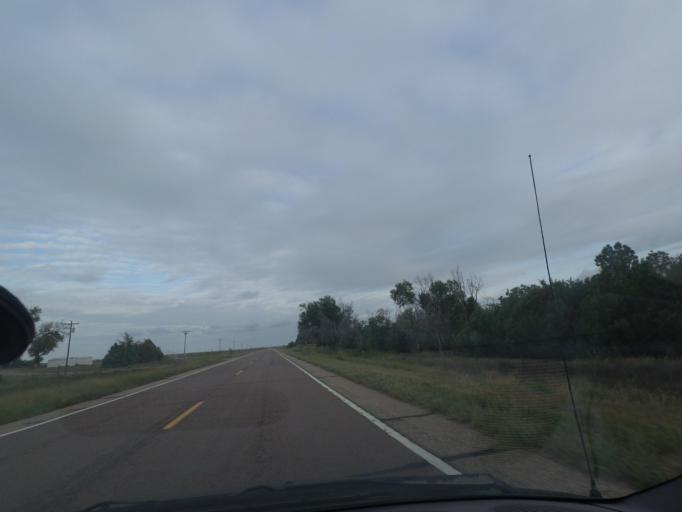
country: US
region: Colorado
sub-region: Kit Carson County
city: Burlington
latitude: 39.6580
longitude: -102.5382
